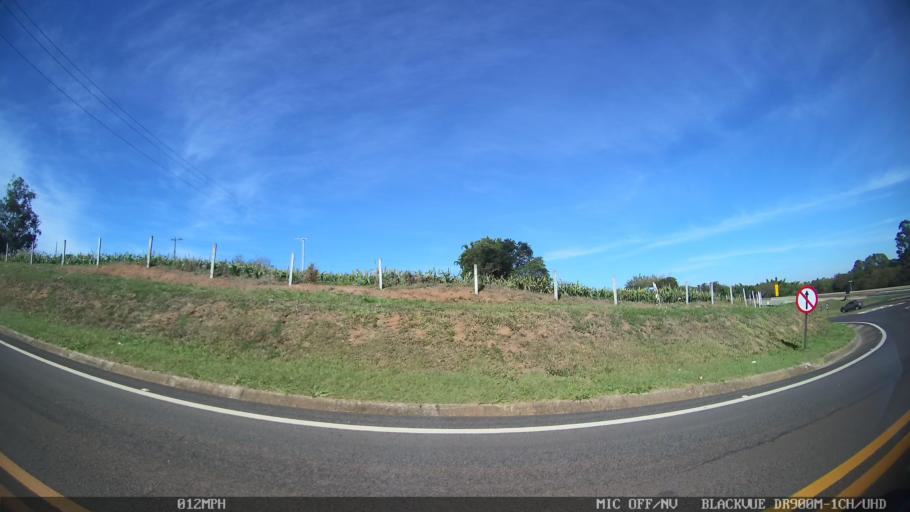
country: BR
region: Sao Paulo
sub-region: Pirassununga
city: Pirassununga
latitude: -22.0730
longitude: -47.4225
